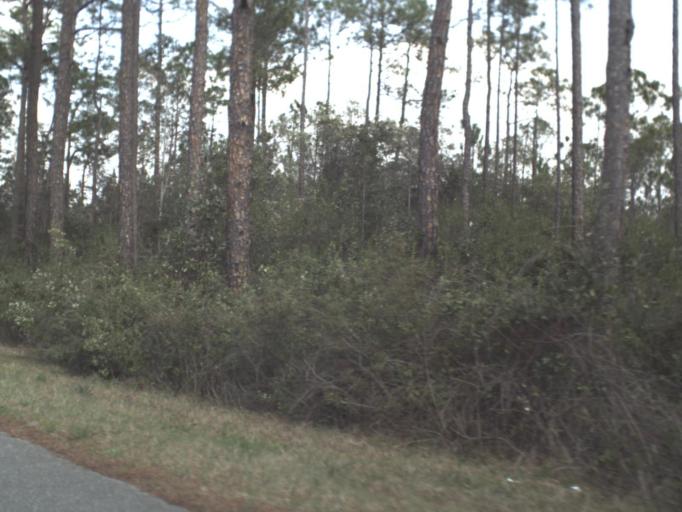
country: US
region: Florida
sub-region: Franklin County
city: Apalachicola
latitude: 29.9743
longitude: -84.9749
